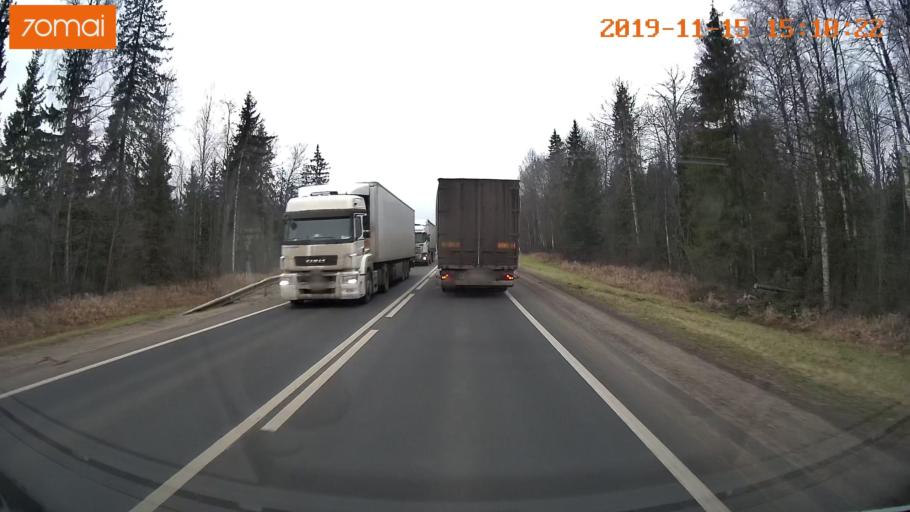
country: RU
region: Jaroslavl
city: Prechistoye
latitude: 58.3486
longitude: 40.2546
